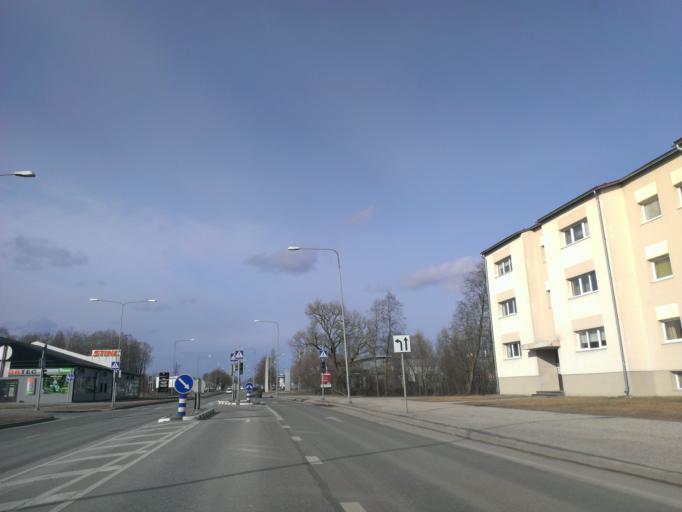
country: EE
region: Paernumaa
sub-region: Paernu linn
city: Parnu
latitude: 58.4039
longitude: 24.4930
